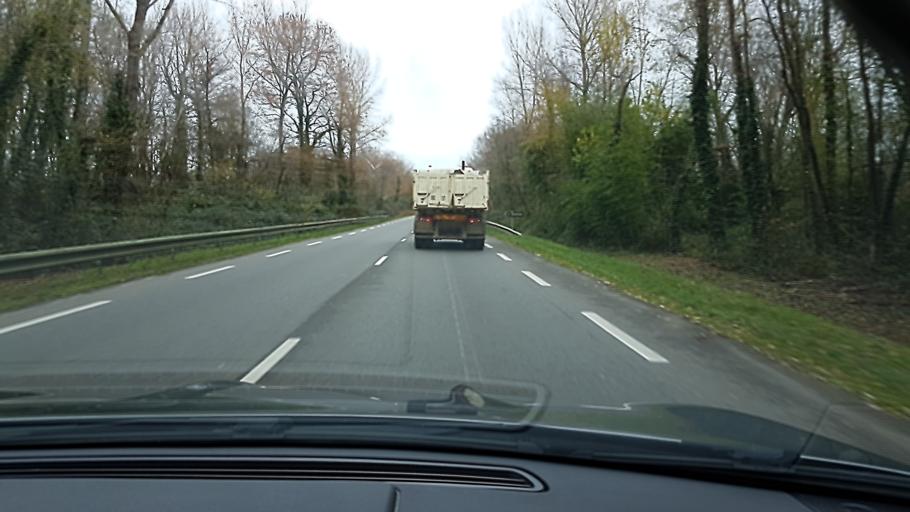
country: FR
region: Aquitaine
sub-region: Departement des Pyrenees-Atlantiques
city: Idron
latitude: 43.3098
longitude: -0.3059
